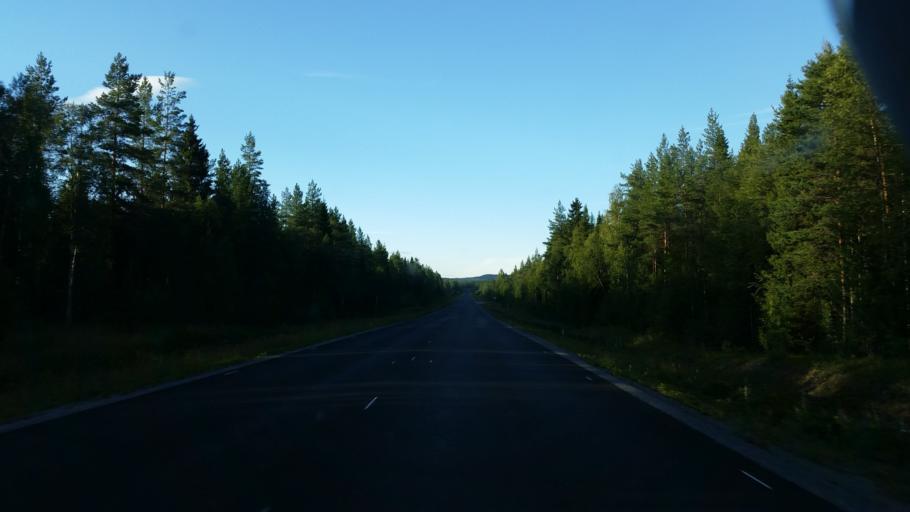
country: SE
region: Vaesterbotten
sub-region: Dorotea Kommun
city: Dorotea
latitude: 64.2588
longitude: 16.4863
